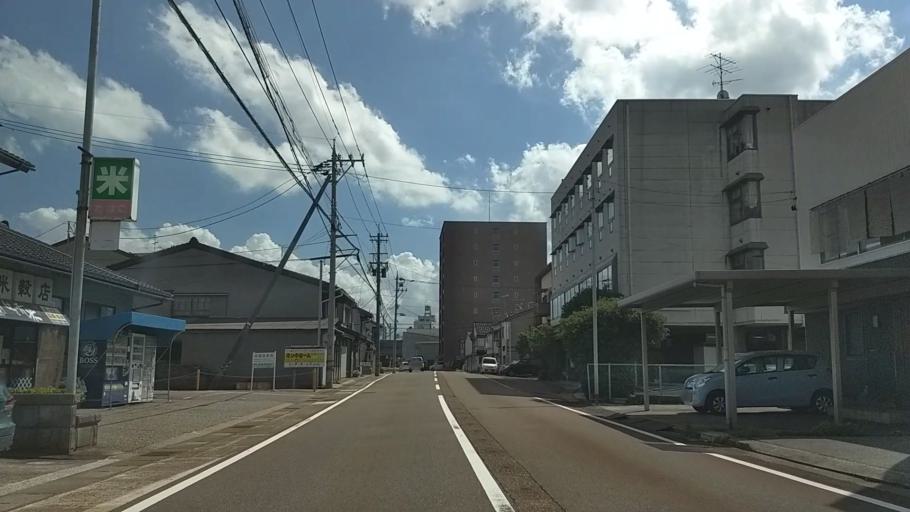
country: JP
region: Ishikawa
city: Kanazawa-shi
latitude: 36.5851
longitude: 136.6516
